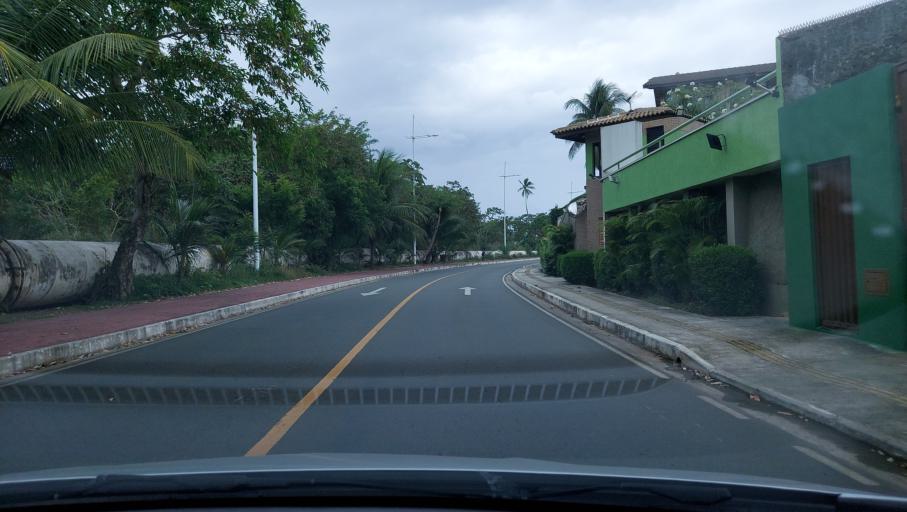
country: BR
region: Bahia
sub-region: Lauro De Freitas
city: Lauro de Freitas
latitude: -12.9535
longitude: -38.3955
